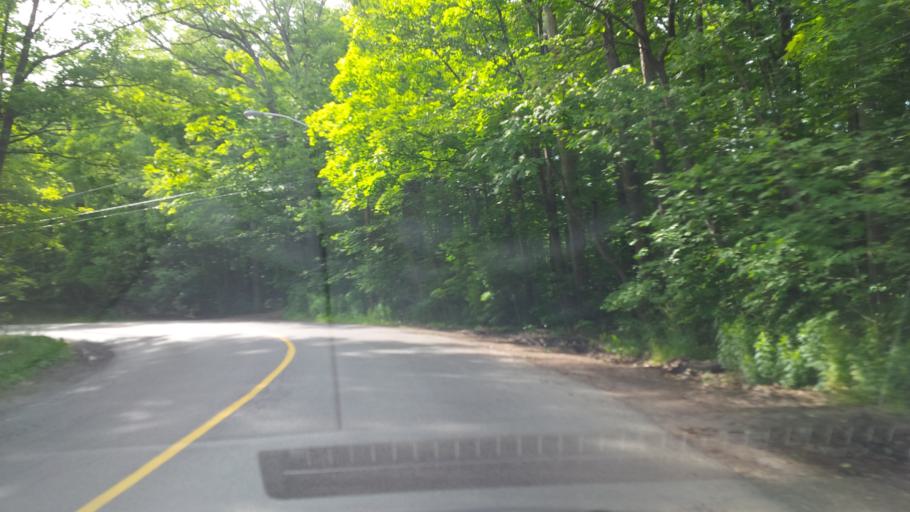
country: CA
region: Ontario
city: Burlington
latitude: 43.3381
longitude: -79.8662
